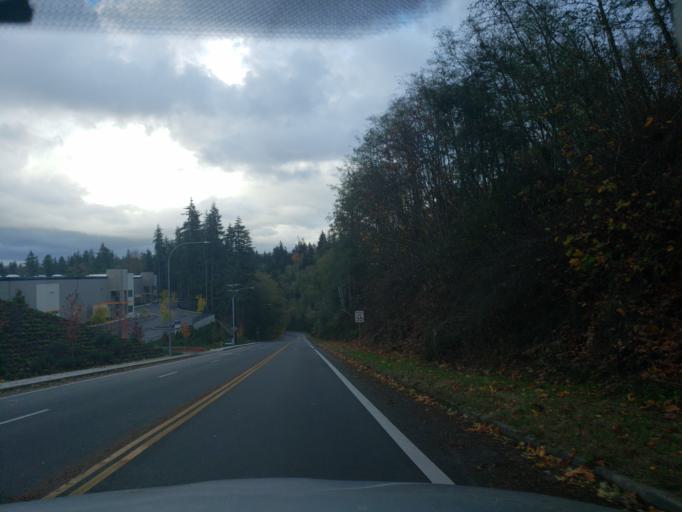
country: US
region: Washington
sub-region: Snohomish County
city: Mukilteo
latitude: 47.9388
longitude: -122.2812
